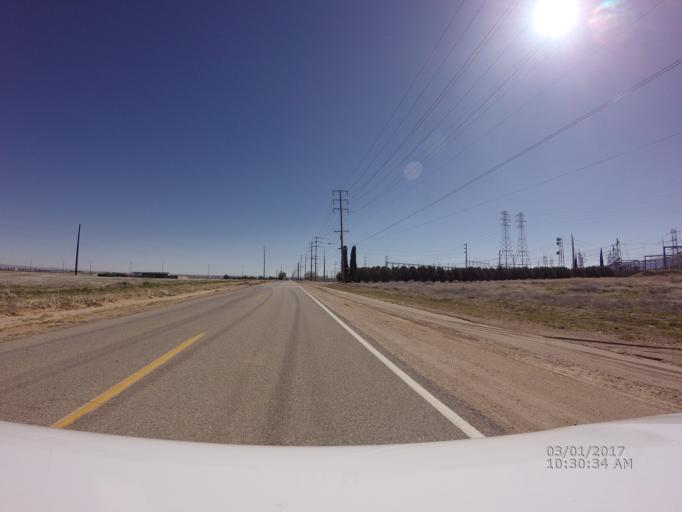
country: US
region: California
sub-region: Los Angeles County
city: Leona Valley
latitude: 34.6892
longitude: -118.3020
